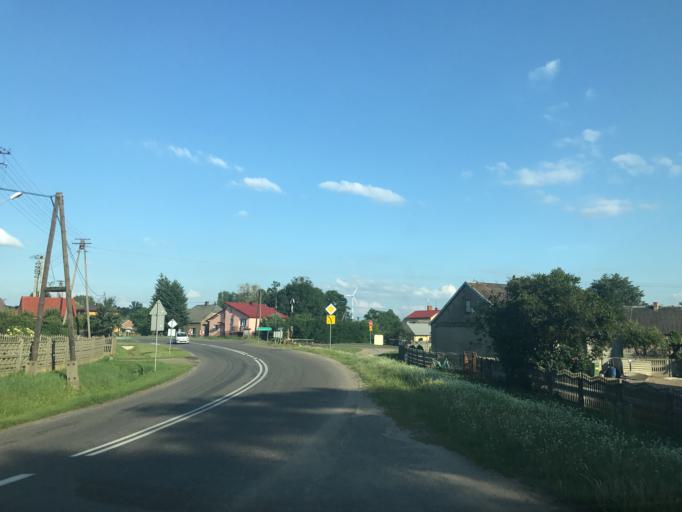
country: PL
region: Greater Poland Voivodeship
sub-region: Powiat turecki
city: Wladyslawow
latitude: 52.1175
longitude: 18.4343
